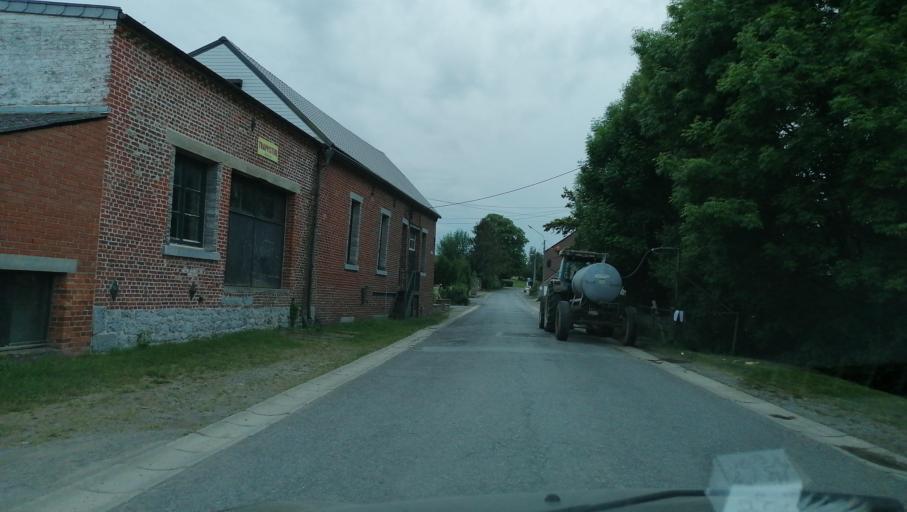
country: BE
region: Wallonia
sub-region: Province du Hainaut
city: Beaumont
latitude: 50.2023
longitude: 4.1707
